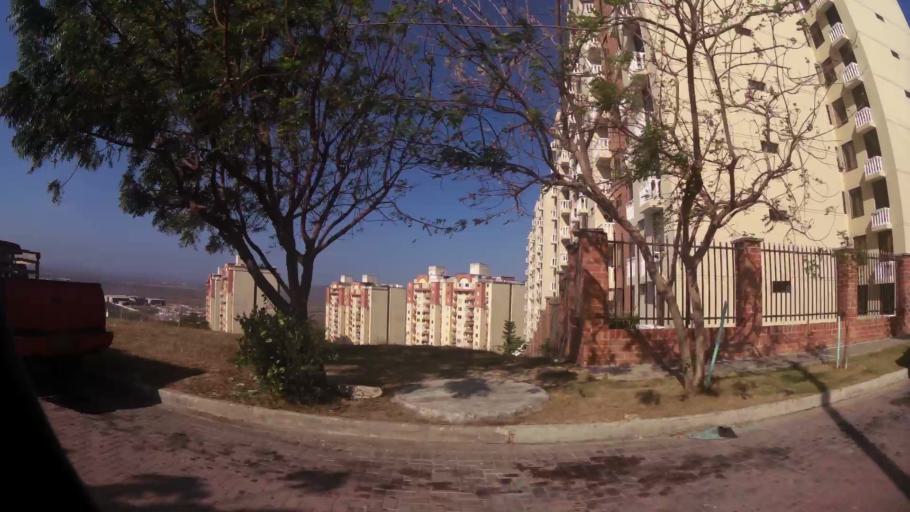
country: CO
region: Atlantico
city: Barranquilla
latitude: 10.9983
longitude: -74.8349
